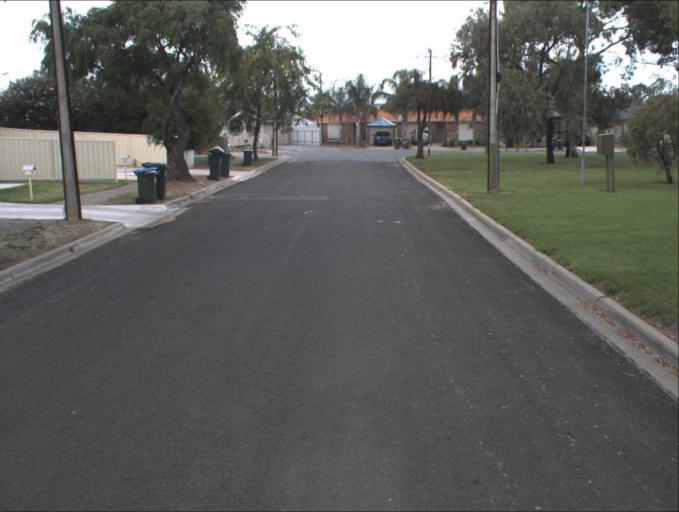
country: AU
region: South Australia
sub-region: Port Adelaide Enfield
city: Gilles Plains
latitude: -34.8499
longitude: 138.6559
